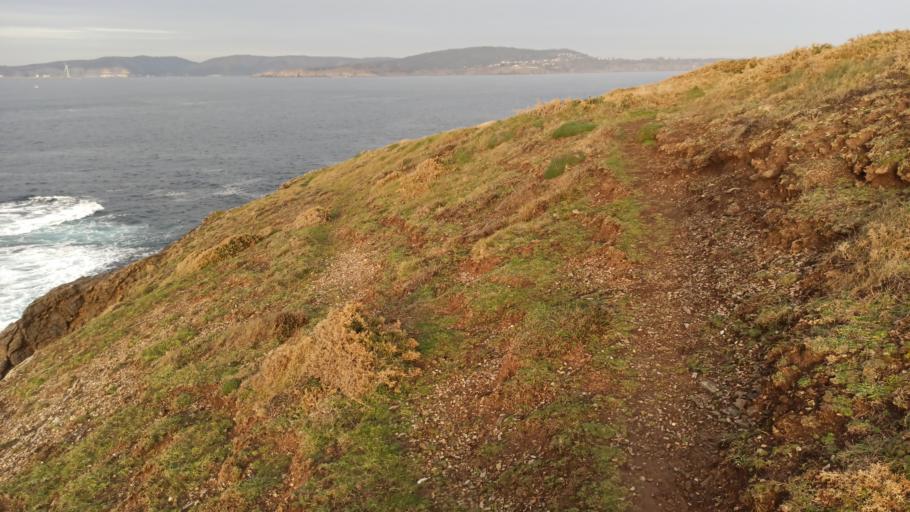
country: ES
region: Galicia
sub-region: Provincia da Coruna
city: A Coruna
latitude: 43.4004
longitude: -8.3342
